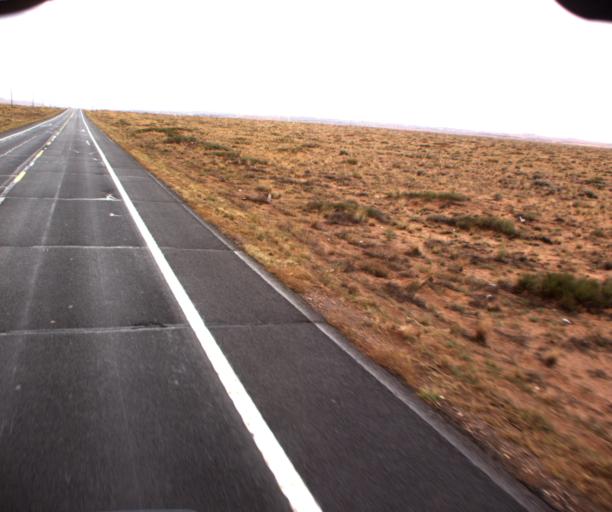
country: US
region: Arizona
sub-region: Coconino County
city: Tuba City
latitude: 36.1421
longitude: -111.1573
